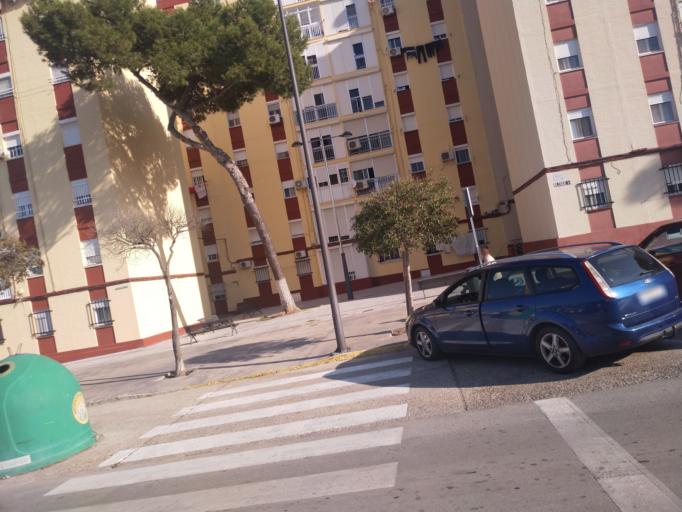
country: ES
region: Andalusia
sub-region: Provincia de Cadiz
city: San Fernando
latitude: 36.4708
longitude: -6.2007
